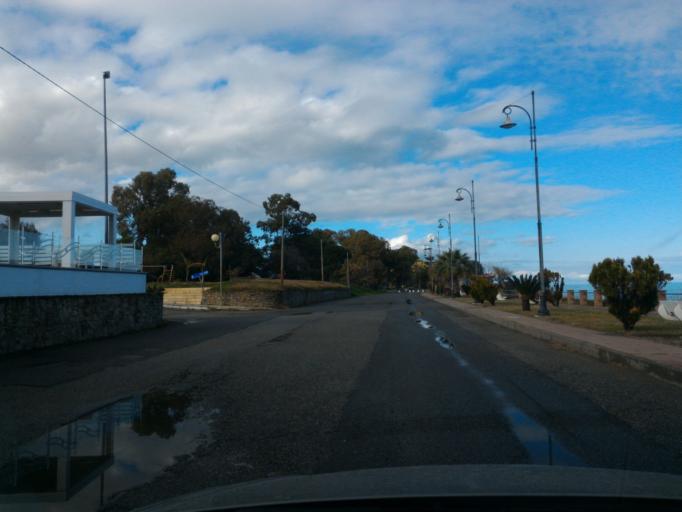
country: IT
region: Calabria
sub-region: Provincia di Crotone
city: Torretta
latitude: 39.4551
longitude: 17.0378
